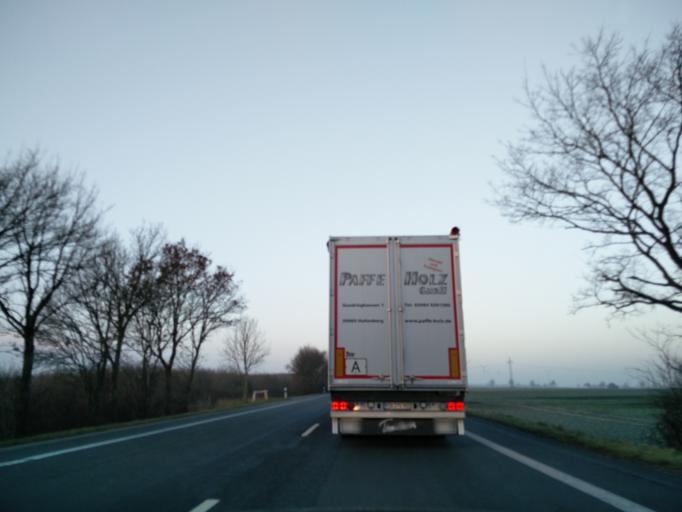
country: DE
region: North Rhine-Westphalia
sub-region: Regierungsbezirk Detmold
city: Buren
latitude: 51.5781
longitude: 8.5562
